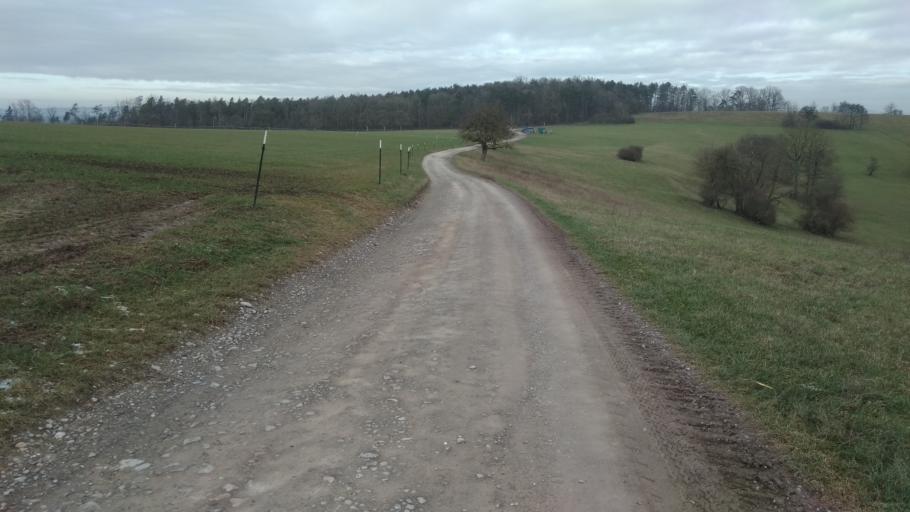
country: DE
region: Baden-Wuerttemberg
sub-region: Karlsruhe Region
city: Mosbach
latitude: 49.3587
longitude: 9.1753
